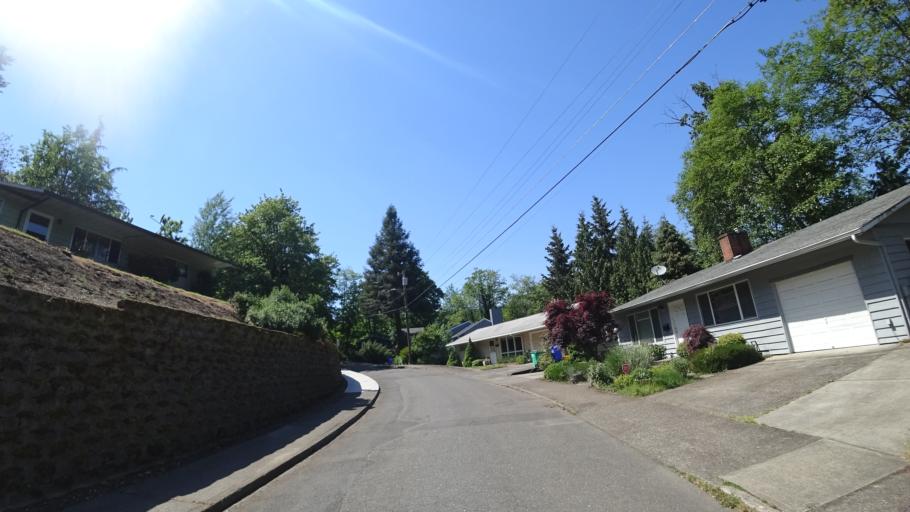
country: US
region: Oregon
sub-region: Clackamas County
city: Lake Oswego
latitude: 45.4691
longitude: -122.6848
